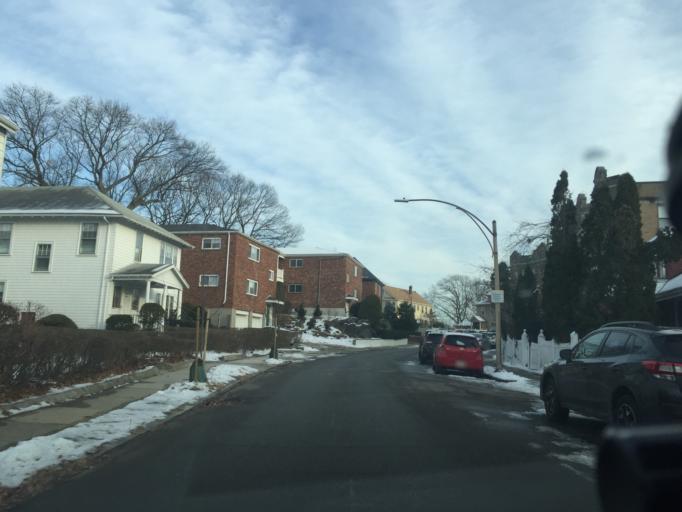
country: US
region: Massachusetts
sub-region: Norfolk County
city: Brookline
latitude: 42.3430
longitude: -71.1494
